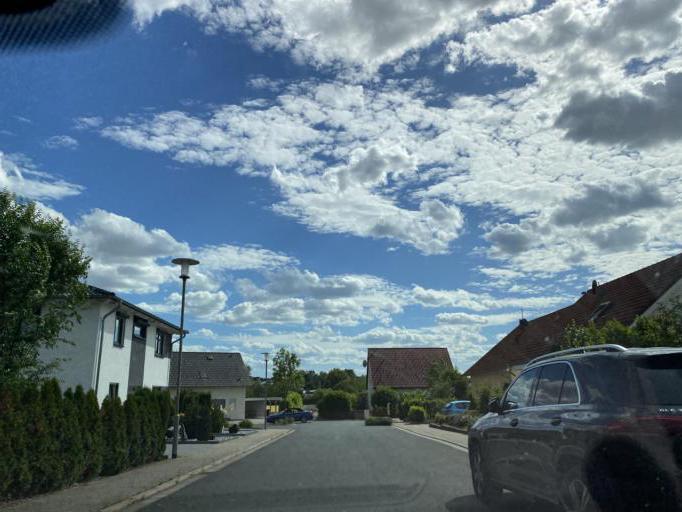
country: DE
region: Rheinland-Pfalz
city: Sprendlingen
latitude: 49.8662
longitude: 7.9823
